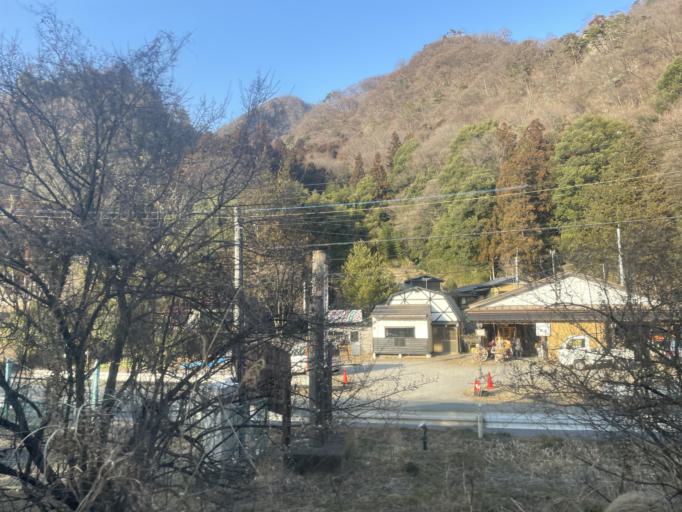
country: JP
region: Gunma
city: Nakanojomachi
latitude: 36.5654
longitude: 138.8937
